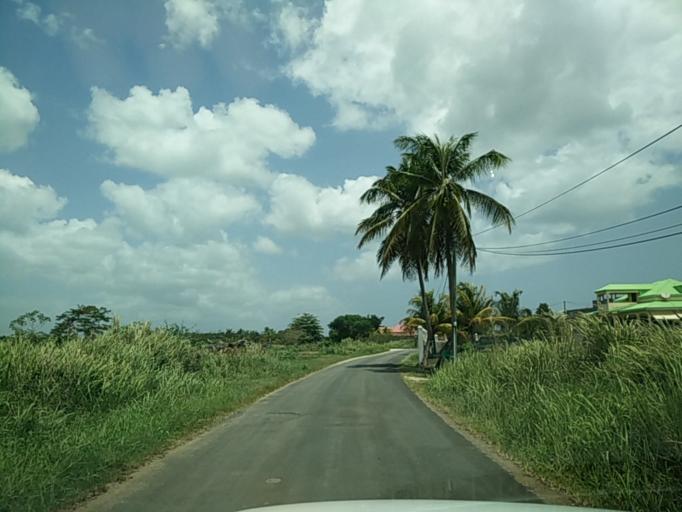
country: GP
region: Guadeloupe
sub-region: Guadeloupe
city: Les Abymes
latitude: 16.2840
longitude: -61.5222
